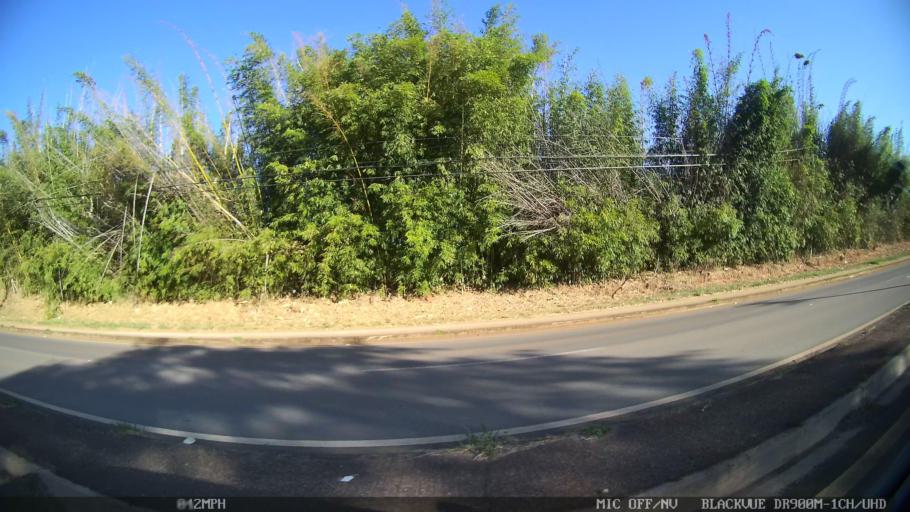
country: BR
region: Sao Paulo
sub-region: Nova Odessa
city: Nova Odessa
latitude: -22.7669
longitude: -47.2683
